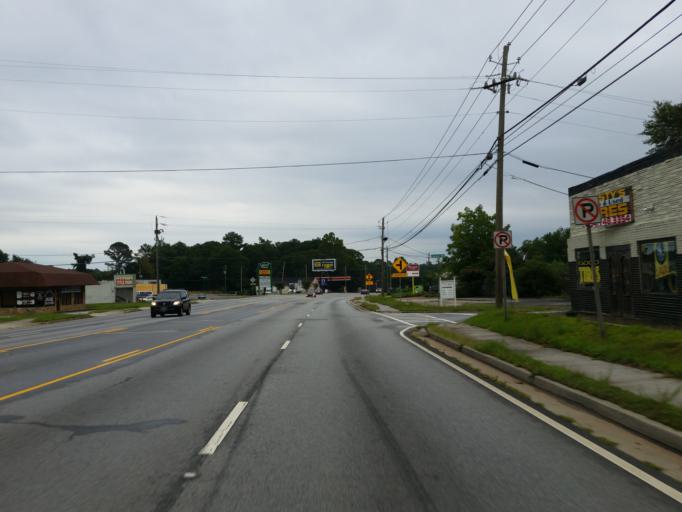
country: US
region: Georgia
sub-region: Cobb County
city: Mableton
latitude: 33.8156
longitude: -84.5643
